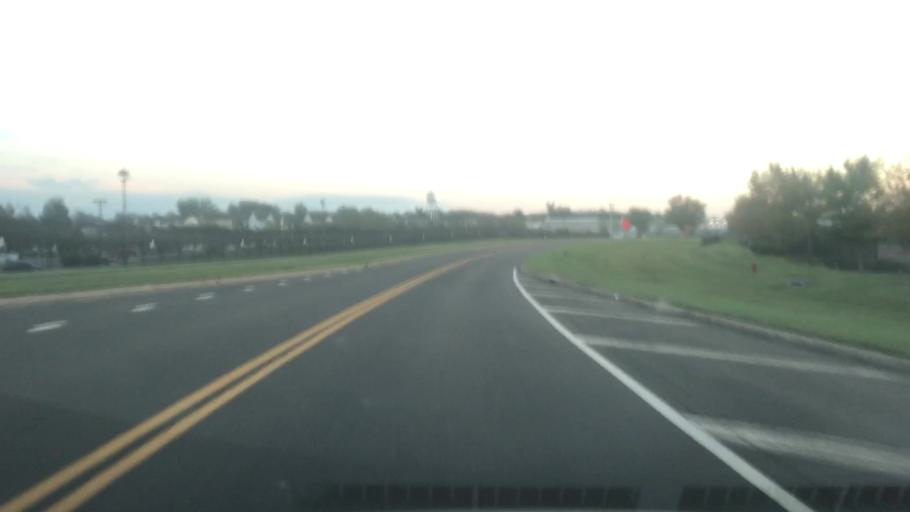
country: US
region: Virginia
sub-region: Fauquier County
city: New Baltimore
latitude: 38.7488
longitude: -77.6724
